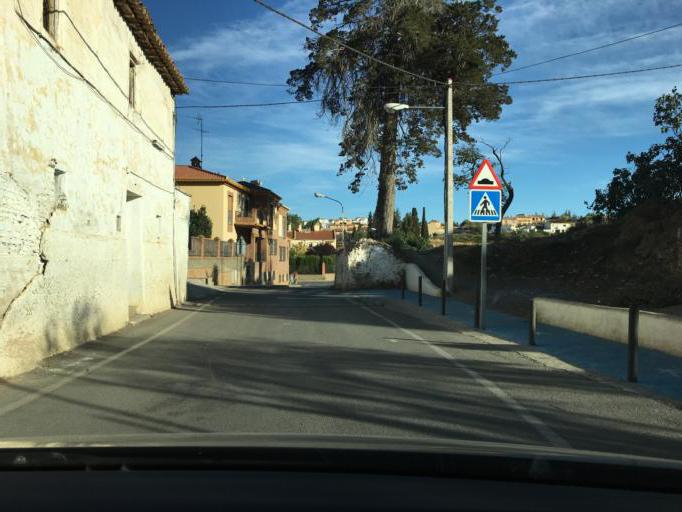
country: ES
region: Andalusia
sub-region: Provincia de Granada
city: Guadix
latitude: 37.2961
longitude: -3.1316
